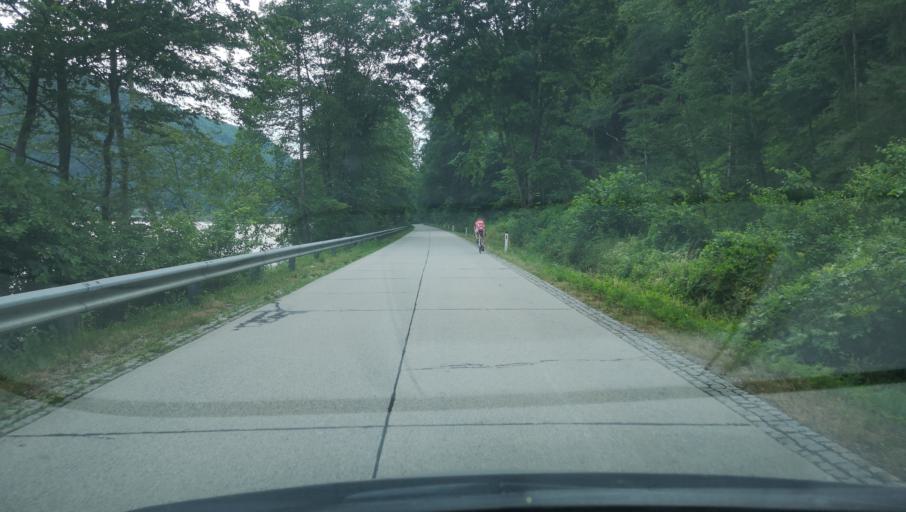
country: AT
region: Lower Austria
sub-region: Politischer Bezirk Melk
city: Nochling
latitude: 48.1938
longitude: 14.9942
